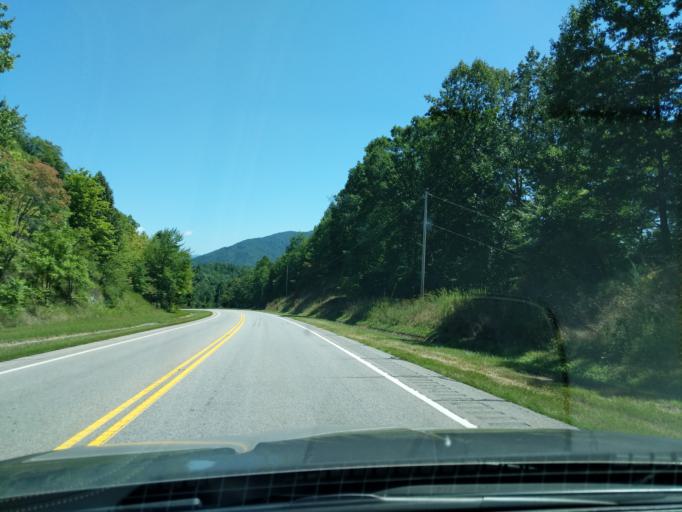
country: US
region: North Carolina
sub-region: Macon County
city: Franklin
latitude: 35.1360
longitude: -83.5098
